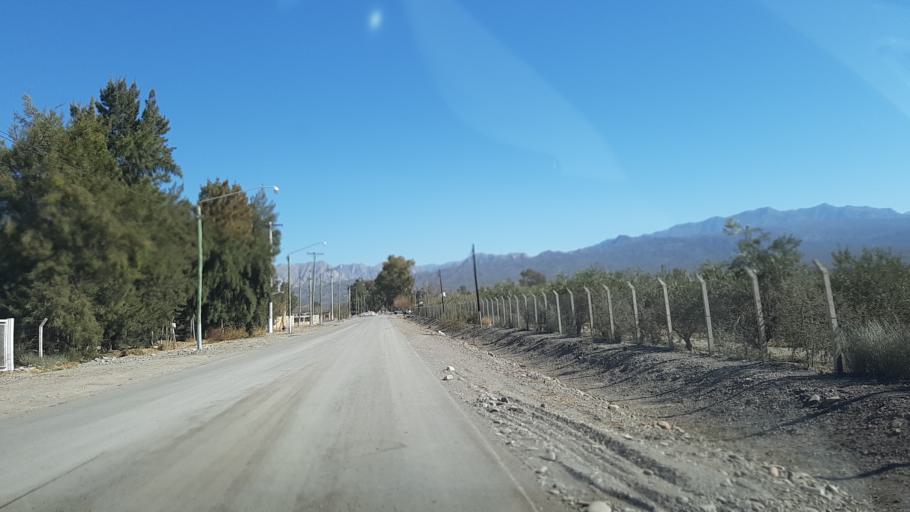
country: AR
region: San Juan
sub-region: Departamento de Zonda
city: Zonda
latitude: -31.4693
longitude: -68.7308
